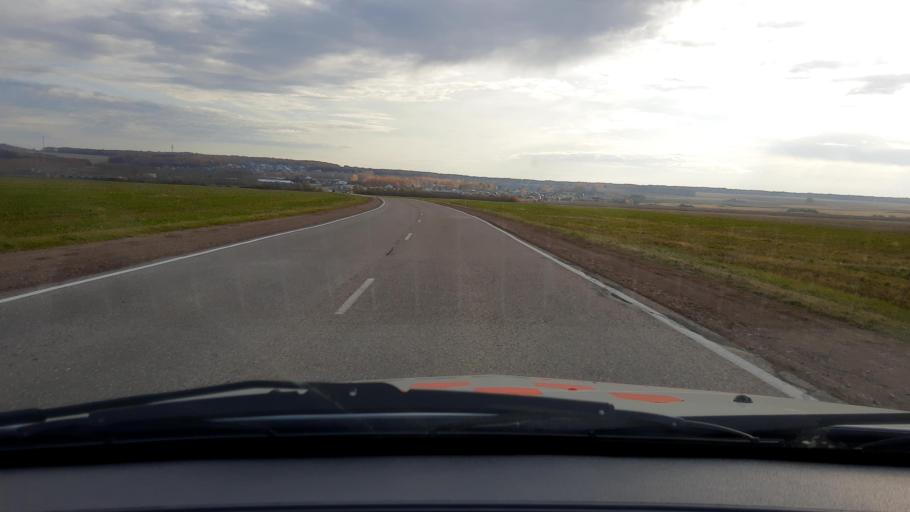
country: RU
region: Bashkortostan
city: Avdon
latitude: 54.8220
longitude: 55.6648
